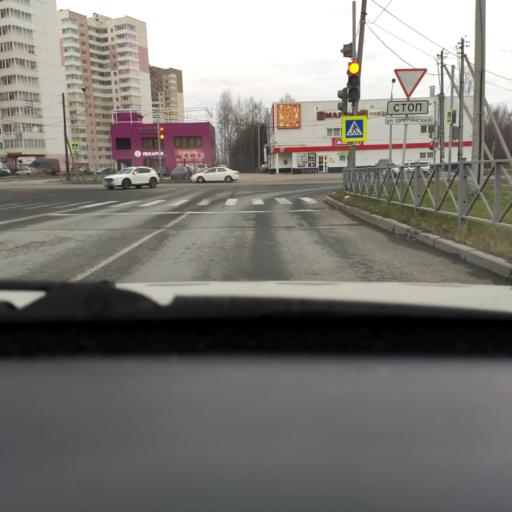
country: RU
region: Perm
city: Polazna
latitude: 58.1329
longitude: 56.4036
